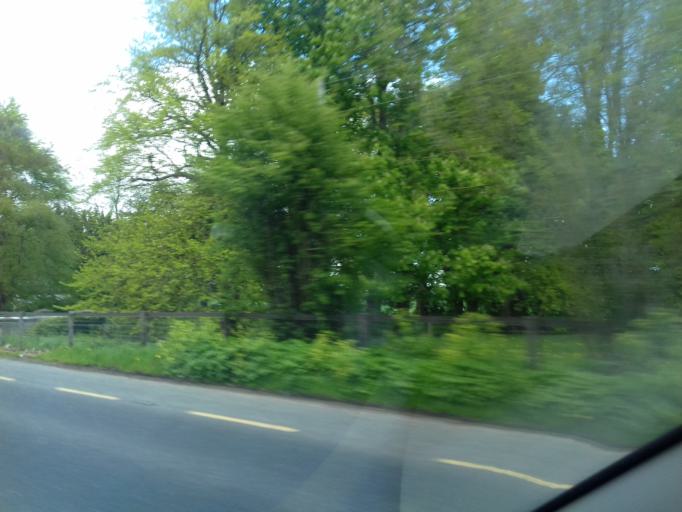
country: IE
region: Leinster
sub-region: Kilkenny
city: Kilkenny
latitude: 52.6235
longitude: -7.2501
